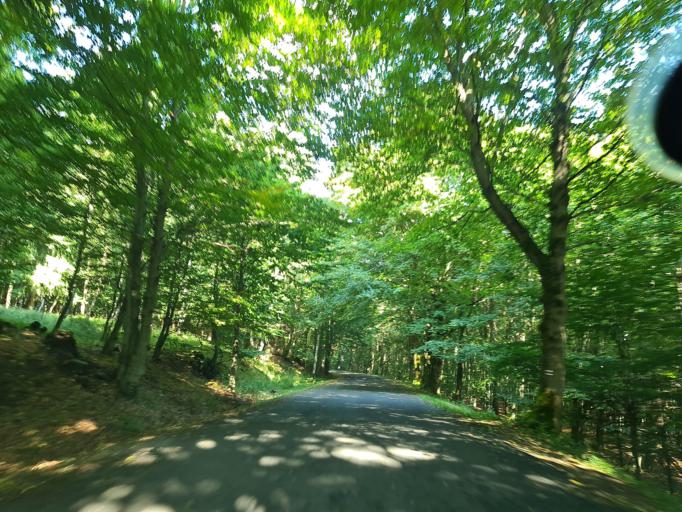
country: CZ
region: Ustecky
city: Horni Jiretin
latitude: 50.6086
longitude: 13.5304
